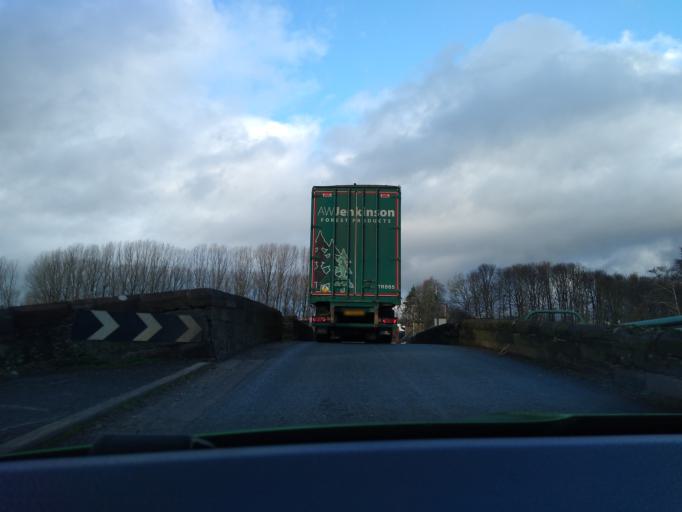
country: GB
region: England
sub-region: Cumbria
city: Penrith
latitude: 54.6514
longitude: -2.7419
